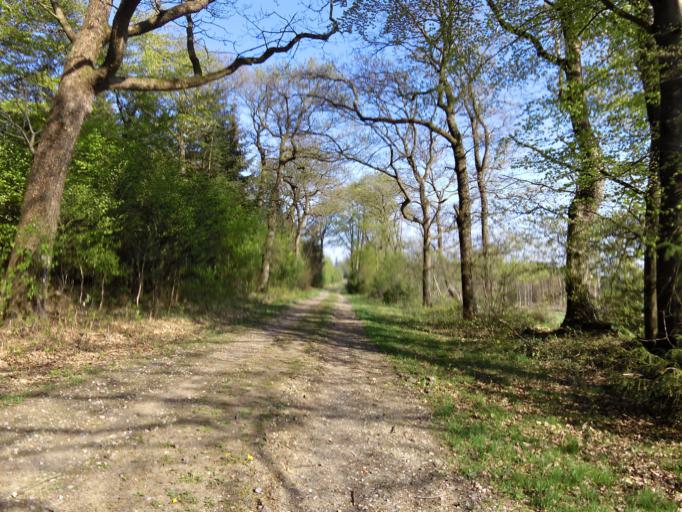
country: DK
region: South Denmark
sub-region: Tonder Kommune
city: Toftlund
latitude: 55.1959
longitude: 8.9396
